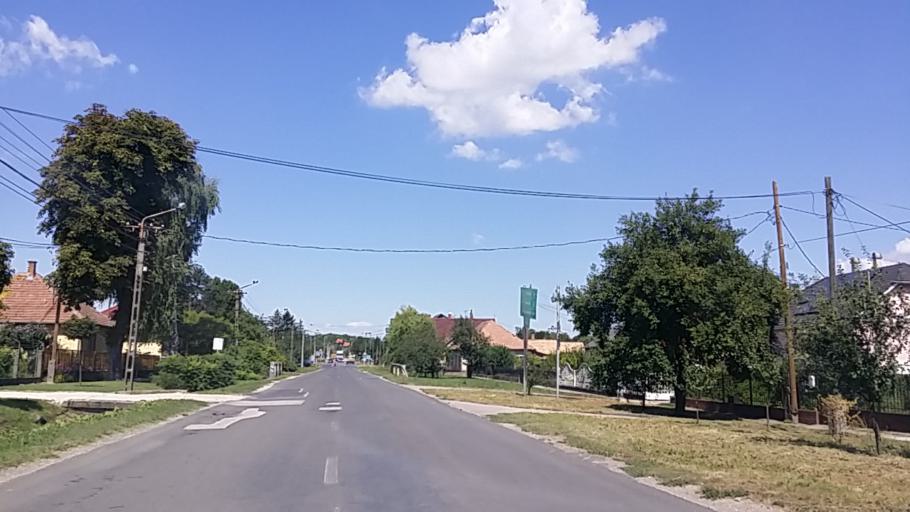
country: HU
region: Tolna
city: Simontornya
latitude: 46.7551
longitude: 18.5448
